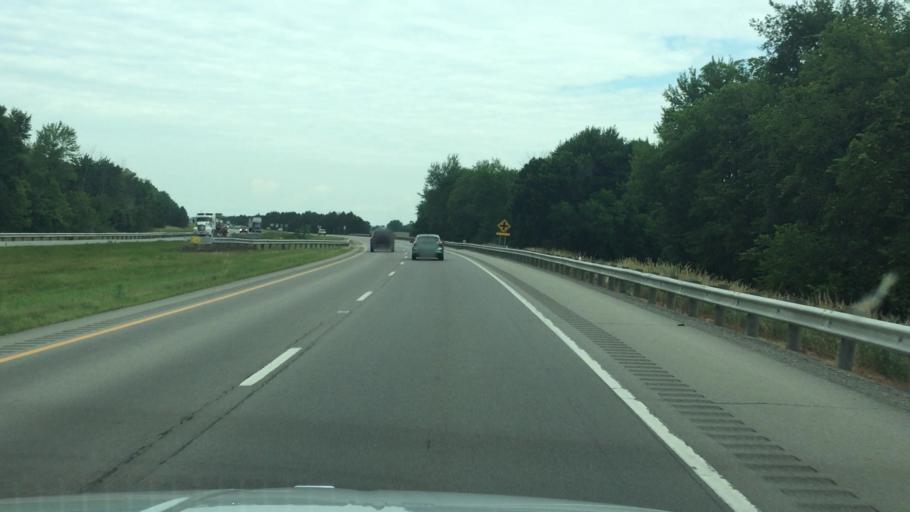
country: US
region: Ohio
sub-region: Wyandot County
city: Carey
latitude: 40.9816
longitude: -83.5001
